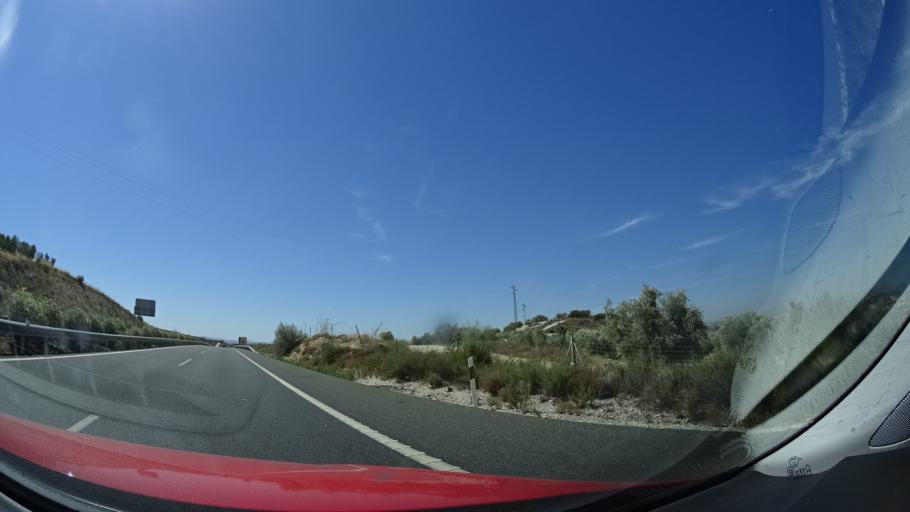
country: ES
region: Andalusia
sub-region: Provincia de Sevilla
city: Gilena
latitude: 37.2837
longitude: -4.9150
